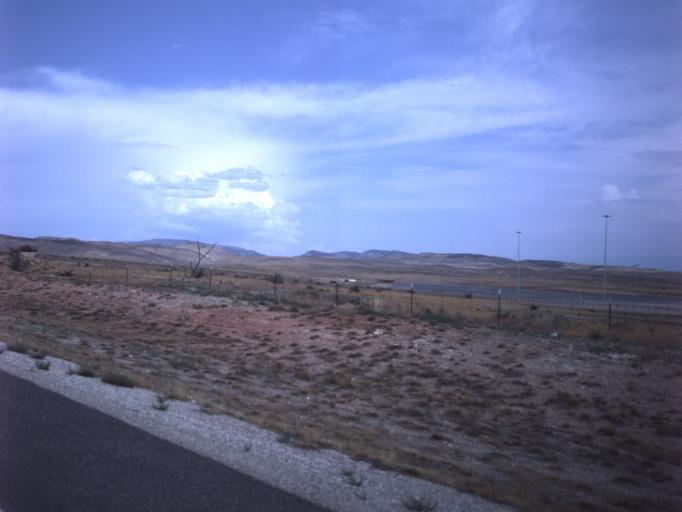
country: US
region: Utah
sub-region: Sanpete County
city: Gunnison
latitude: 39.1645
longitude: -111.8184
